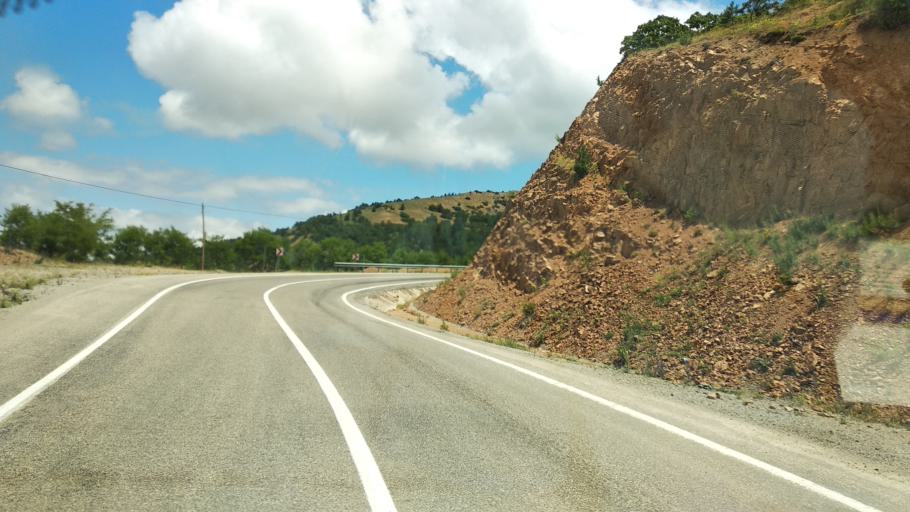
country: TR
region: Gumushane
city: Kose
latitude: 40.2983
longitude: 39.5676
